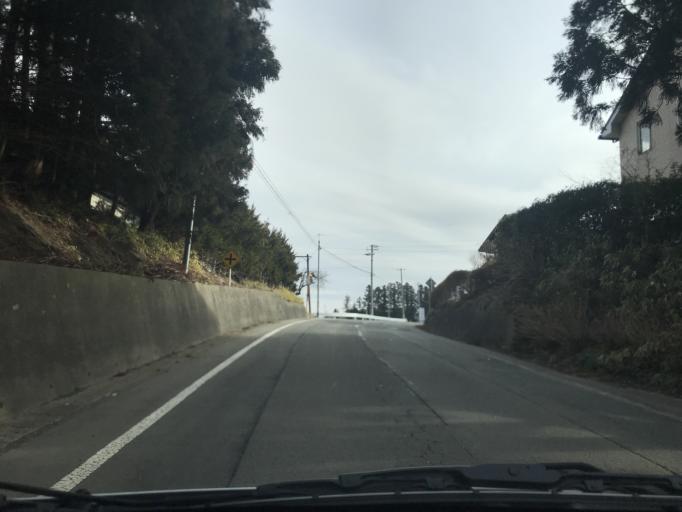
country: JP
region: Iwate
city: Hanamaki
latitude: 39.4203
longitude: 141.0804
